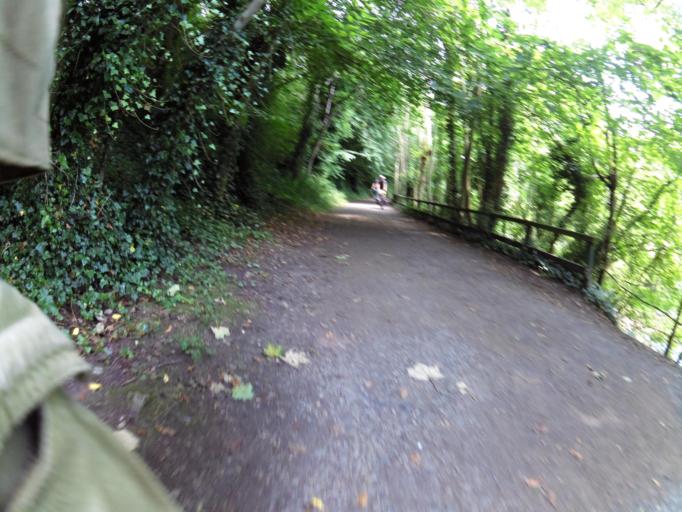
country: GB
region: Scotland
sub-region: Edinburgh
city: Colinton
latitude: 55.9040
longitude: -3.2816
